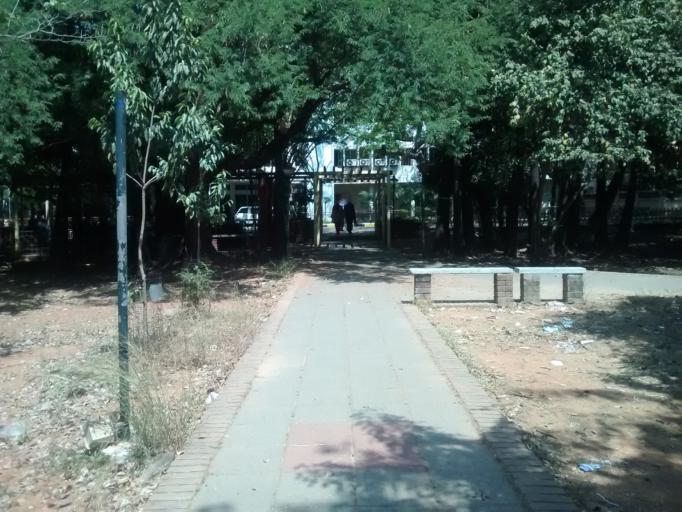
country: IN
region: Tamil Nadu
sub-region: Chennai
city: Gandhi Nagar
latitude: 13.0088
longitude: 80.2357
